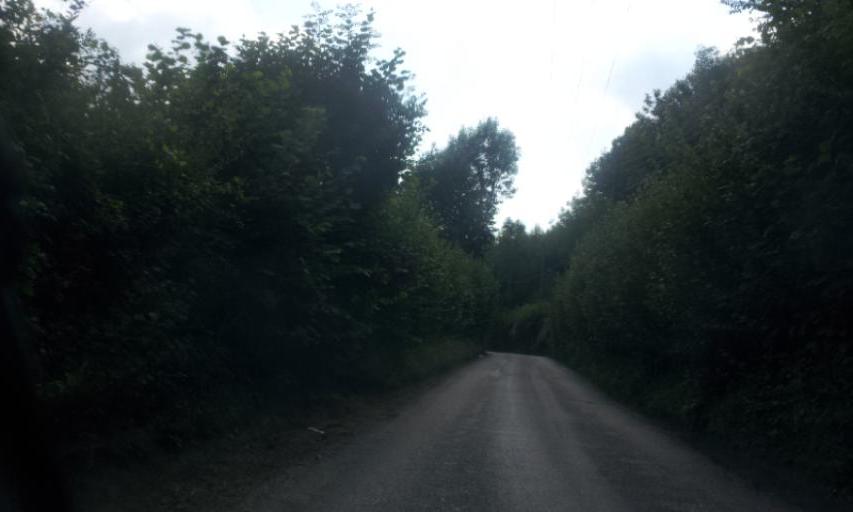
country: GB
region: England
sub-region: Kent
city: Maidstone
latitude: 51.2439
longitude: 0.5021
